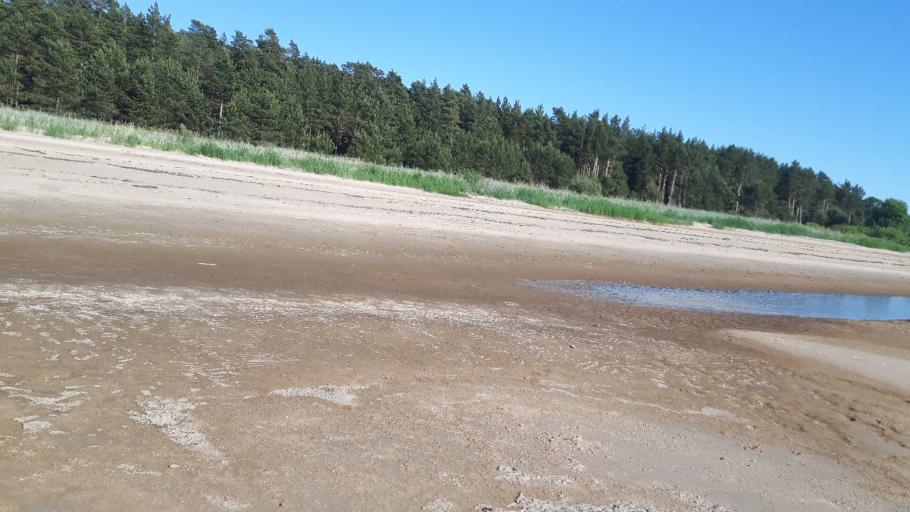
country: LV
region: Salacgrivas
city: Salacgriva
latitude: 57.7079
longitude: 24.3426
